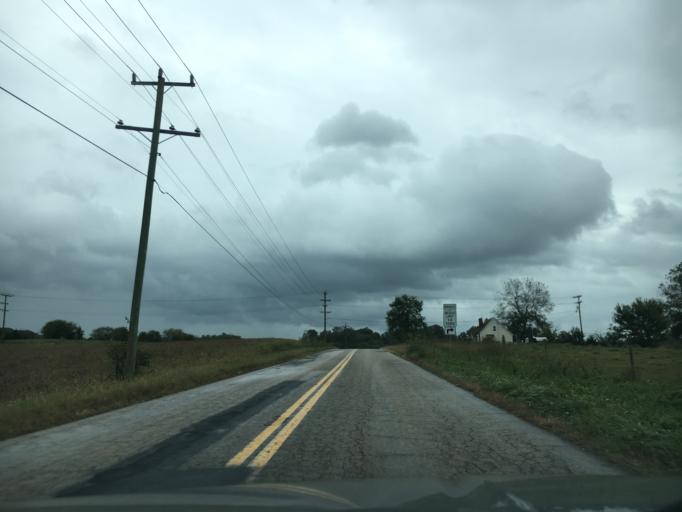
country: US
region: Virginia
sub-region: Amelia County
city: Amelia Court House
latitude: 37.3926
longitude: -77.9753
